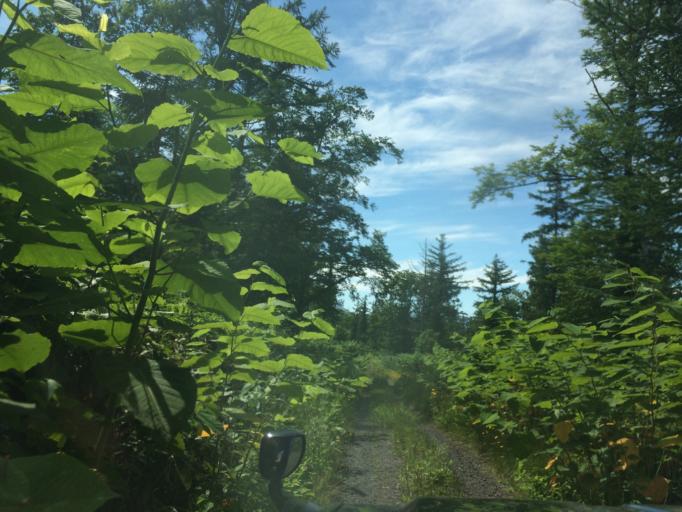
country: JP
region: Hokkaido
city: Niseko Town
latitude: 42.8651
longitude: 140.7978
